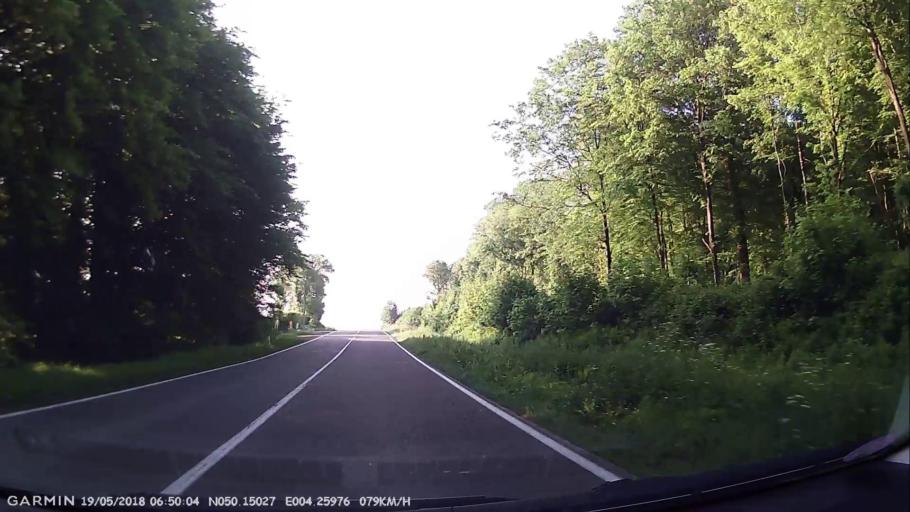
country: BE
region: Wallonia
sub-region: Province du Hainaut
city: Froidchapelle
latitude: 50.1501
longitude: 4.2600
